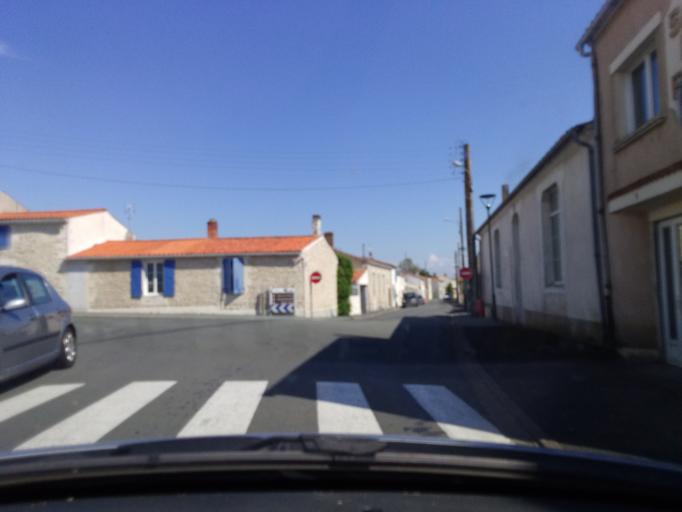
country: FR
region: Pays de la Loire
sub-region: Departement de la Vendee
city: Triaize
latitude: 46.3932
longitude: -1.2017
